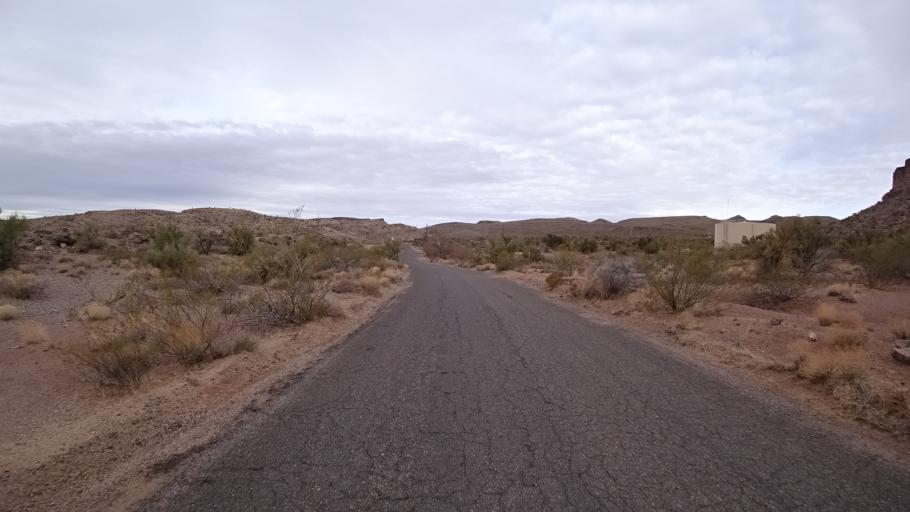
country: US
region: Arizona
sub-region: Mohave County
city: Kingman
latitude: 35.2034
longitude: -114.0784
